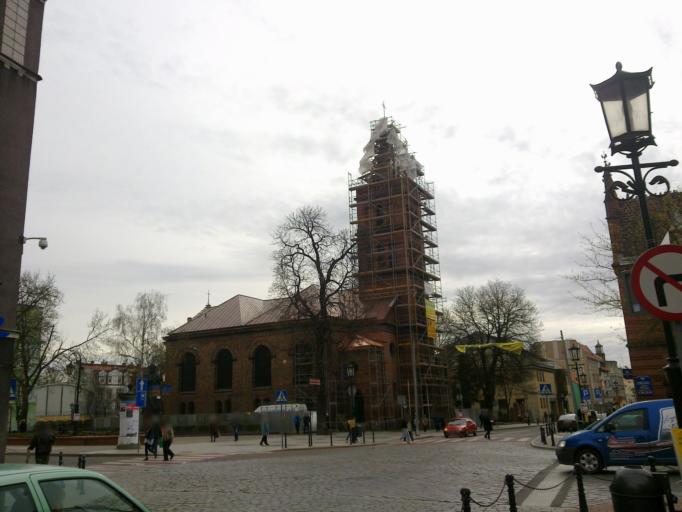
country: PL
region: Greater Poland Voivodeship
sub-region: Powiat gnieznienski
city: Gniezno
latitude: 52.5348
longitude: 17.5998
